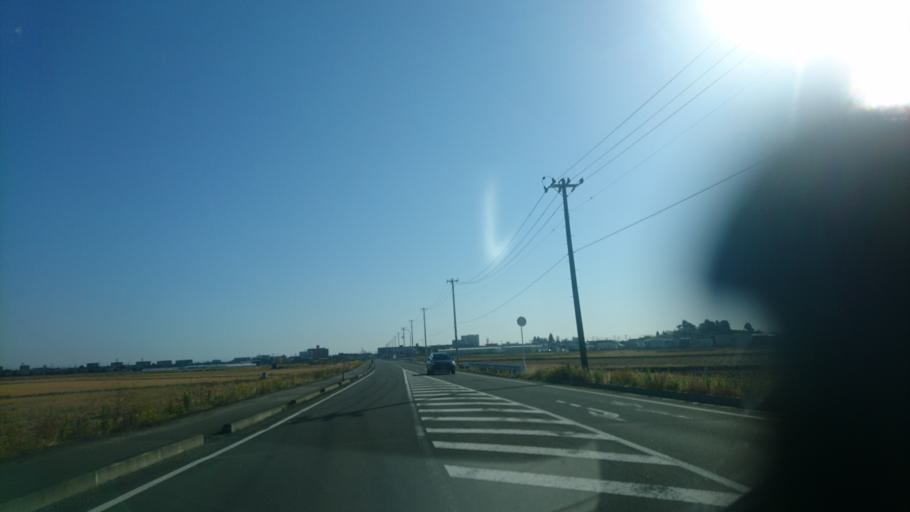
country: JP
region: Miyagi
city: Iwanuma
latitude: 38.1228
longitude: 140.8585
